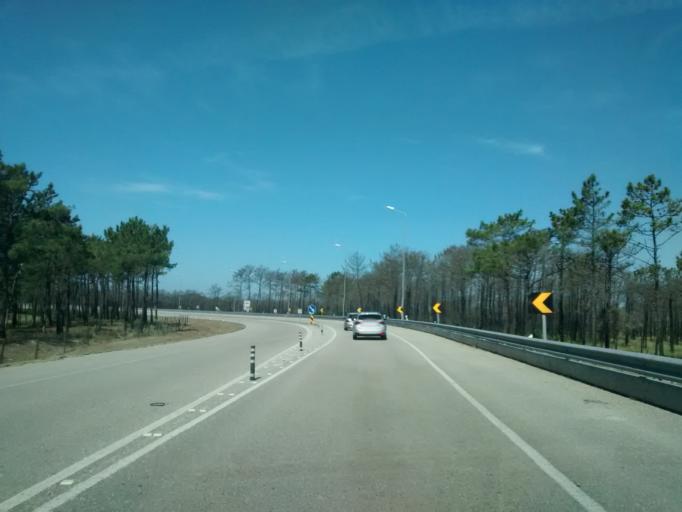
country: PT
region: Coimbra
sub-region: Mira
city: Mira
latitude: 40.4502
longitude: -8.7547
